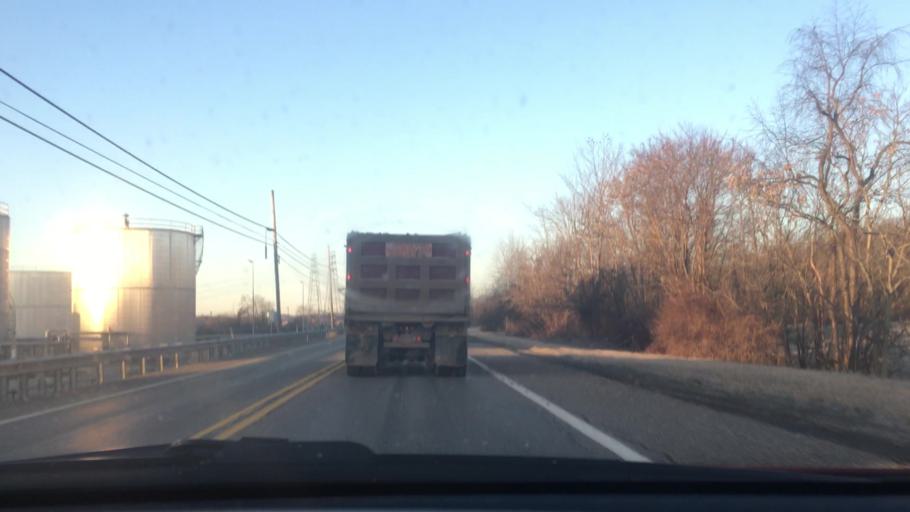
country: US
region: Pennsylvania
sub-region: Allegheny County
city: Elizabeth
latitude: 40.2582
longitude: -79.9165
